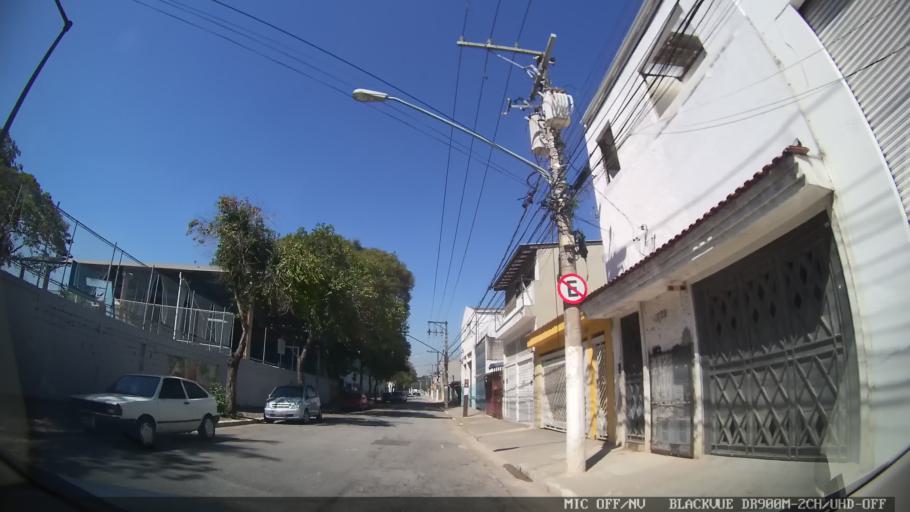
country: BR
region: Sao Paulo
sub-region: Sao Paulo
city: Sao Paulo
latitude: -23.5125
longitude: -46.6507
